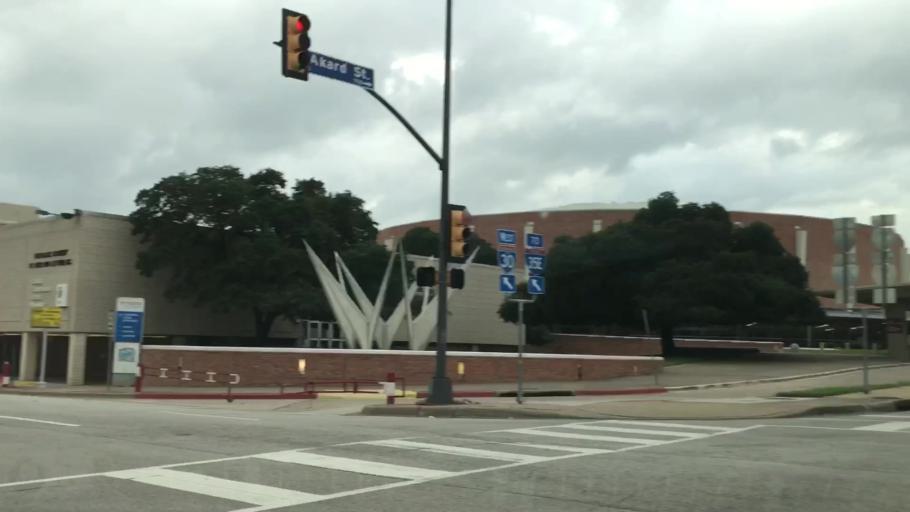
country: US
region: Texas
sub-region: Dallas County
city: Dallas
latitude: 32.7745
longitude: -96.7968
